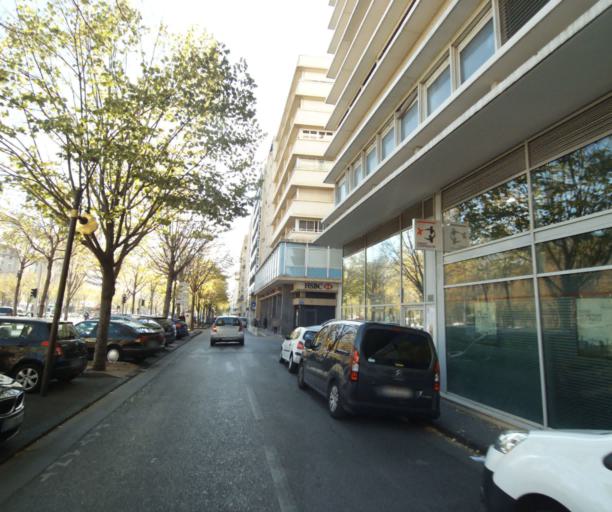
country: FR
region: Provence-Alpes-Cote d'Azur
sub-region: Departement des Bouches-du-Rhone
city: Marseille 08
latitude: 43.2765
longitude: 5.3887
